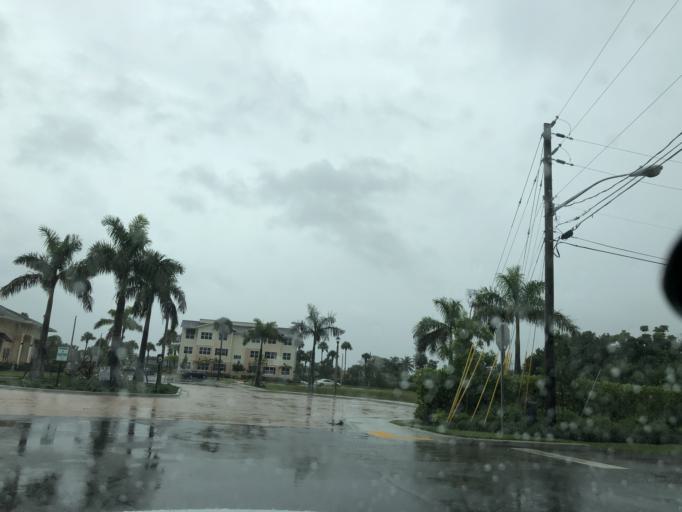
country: US
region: Florida
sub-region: Palm Beach County
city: Plantation Mobile Home Park
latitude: 26.6979
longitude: -80.1260
